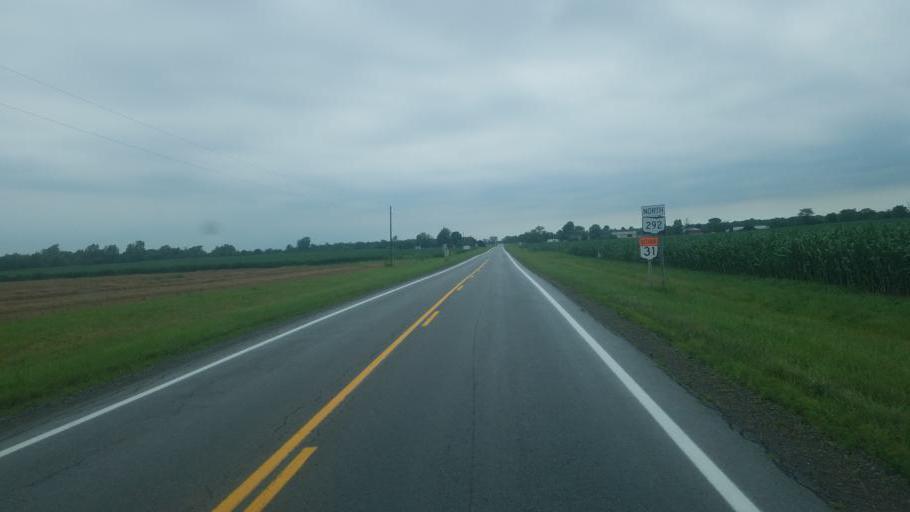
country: US
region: Ohio
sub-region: Hardin County
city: Kenton
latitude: 40.5291
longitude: -83.5755
